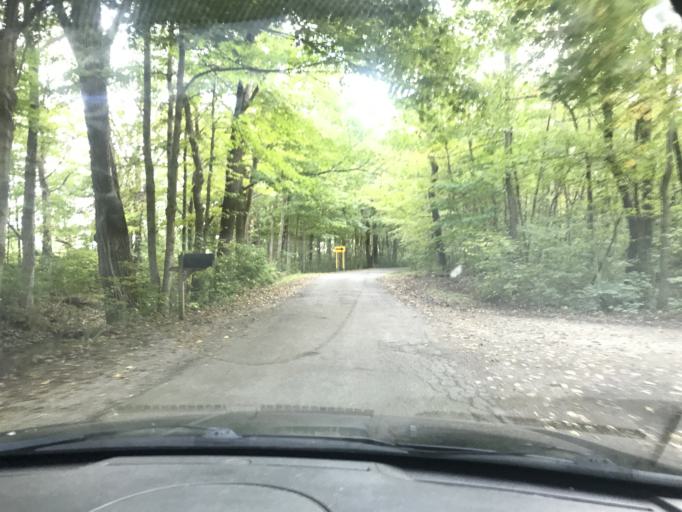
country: US
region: Ohio
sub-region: Logan County
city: West Liberty
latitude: 40.2244
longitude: -83.6713
